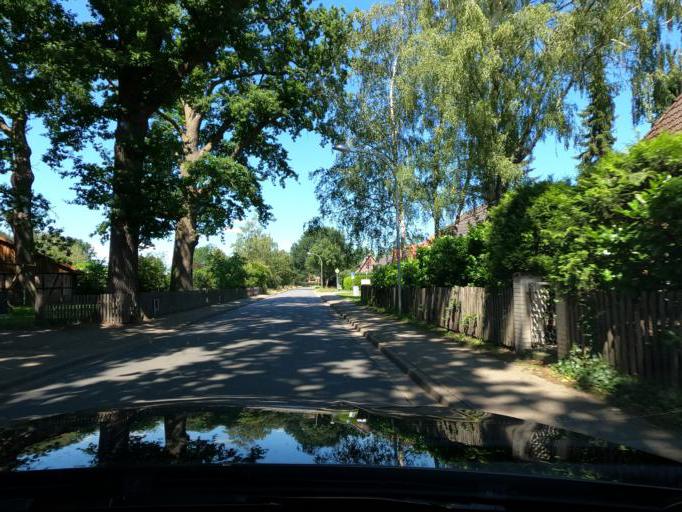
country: DE
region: Lower Saxony
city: Eicklingen
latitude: 52.5525
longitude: 10.1792
